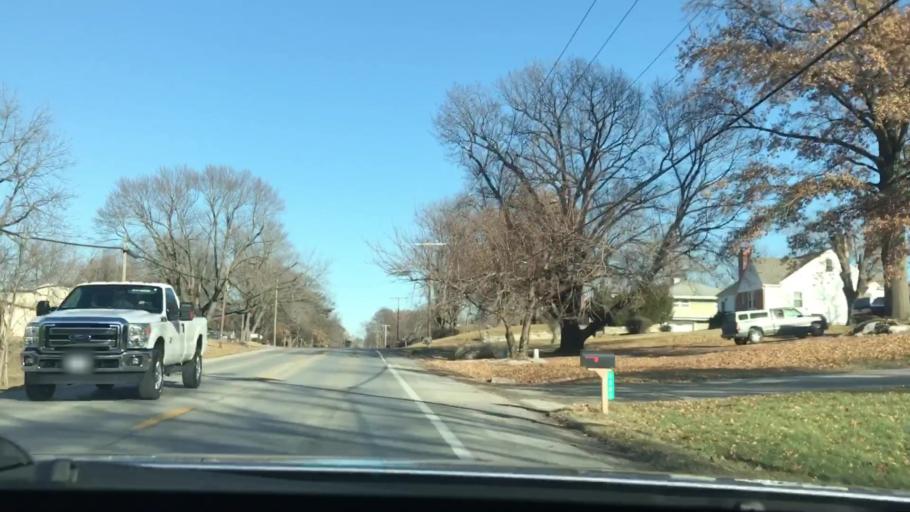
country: US
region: Missouri
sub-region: Platte County
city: Parkville
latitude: 39.2148
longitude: -94.6758
